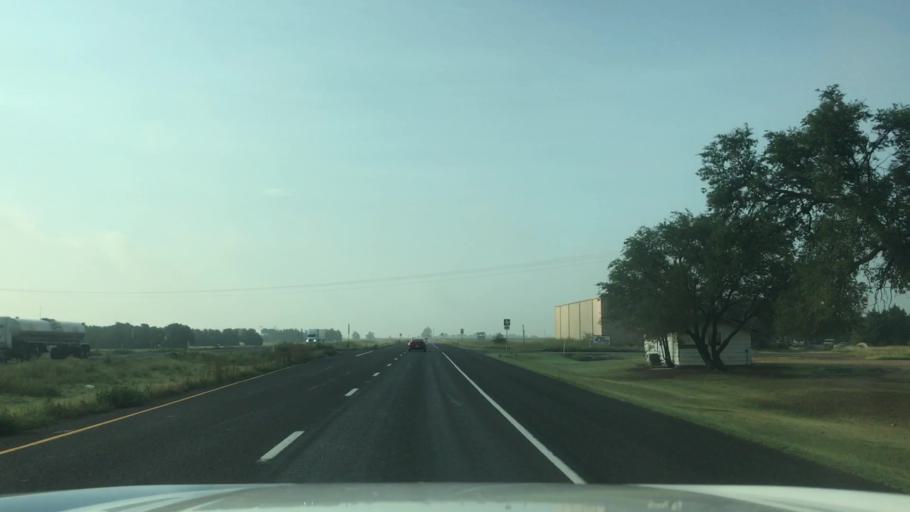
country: US
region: Texas
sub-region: Lubbock County
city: Slaton
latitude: 33.3586
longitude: -101.5558
